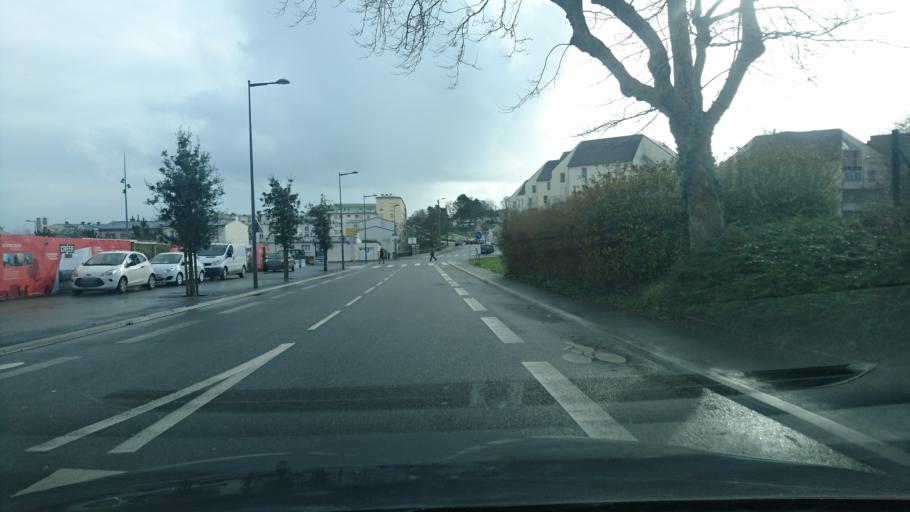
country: FR
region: Brittany
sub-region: Departement du Finistere
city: Brest
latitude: 48.3907
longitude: -4.5037
